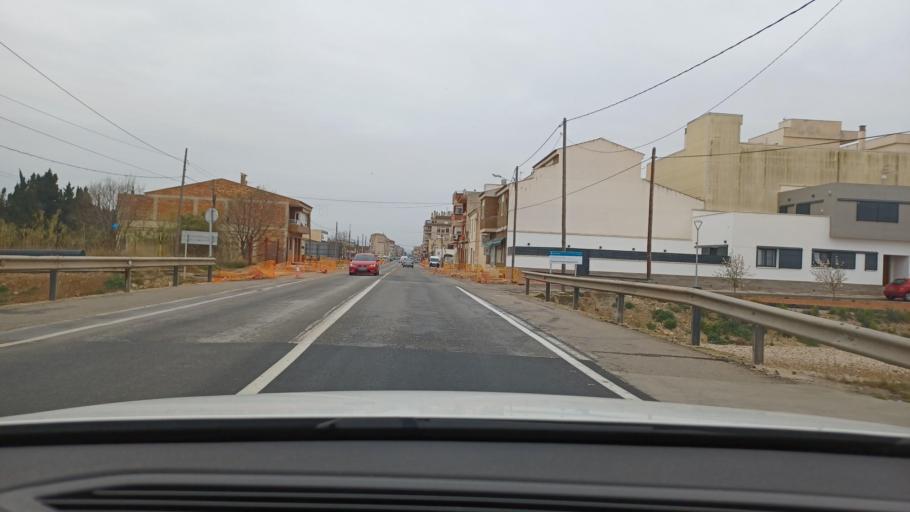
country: ES
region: Catalonia
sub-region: Provincia de Tarragona
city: Amposta
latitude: 40.7449
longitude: 0.6175
